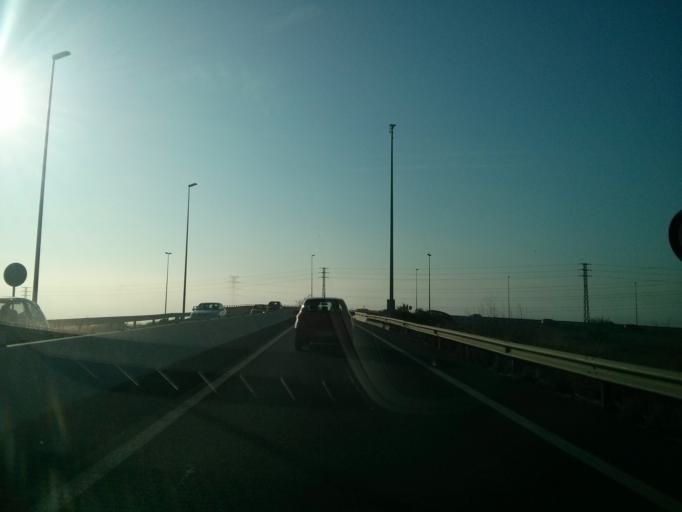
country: ES
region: Valencia
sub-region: Provincia de Valencia
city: Paterna
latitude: 39.4947
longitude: -0.4263
